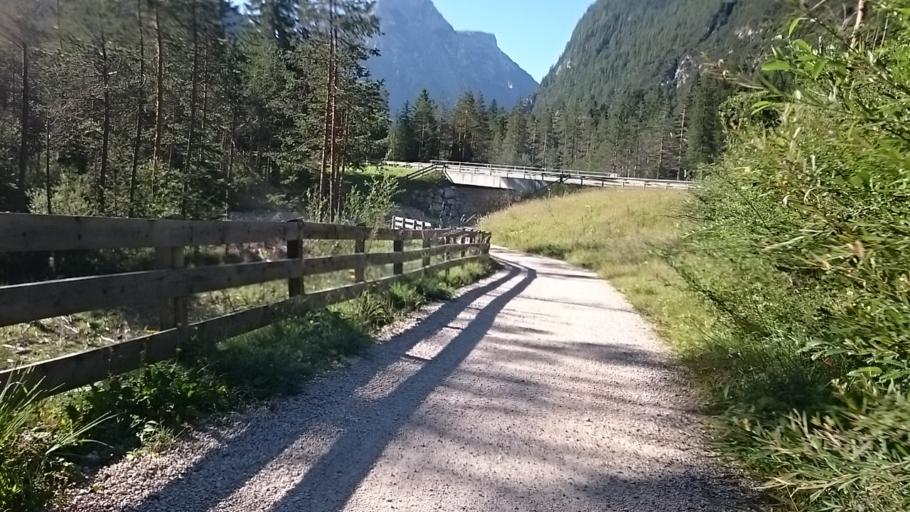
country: IT
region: Trentino-Alto Adige
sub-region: Bolzano
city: Dobbiaco
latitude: 46.6568
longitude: 12.2257
